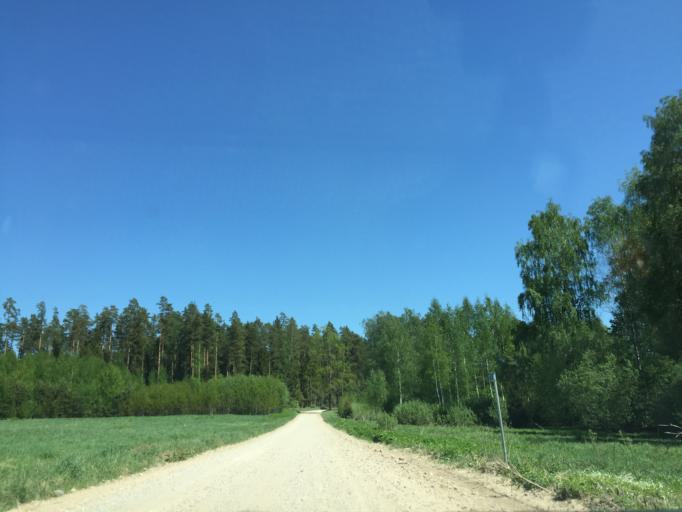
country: LV
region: Ogre
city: Ogre
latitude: 56.7435
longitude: 24.5562
